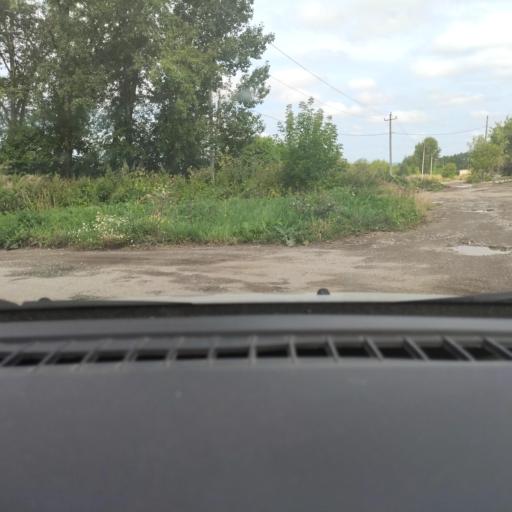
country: RU
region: Perm
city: Lobanovo
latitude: 57.8636
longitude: 56.2820
